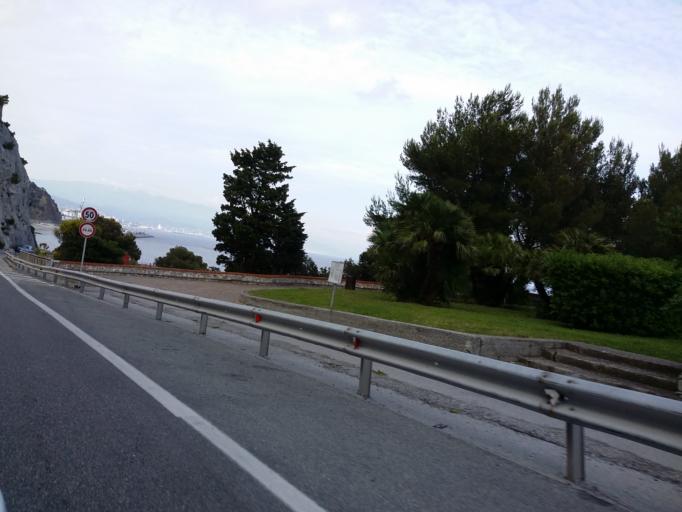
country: IT
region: Liguria
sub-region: Provincia di Savona
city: Bergeggi
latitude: 44.2407
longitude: 8.4442
